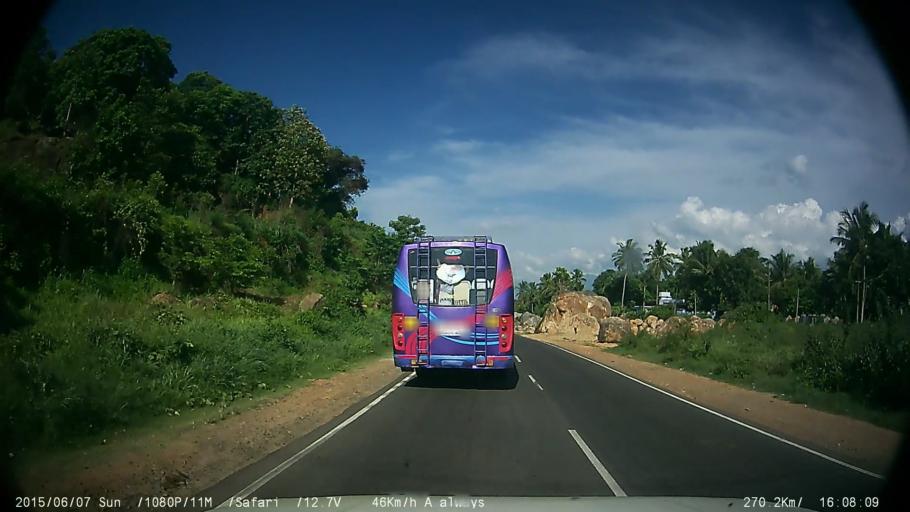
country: IN
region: Kerala
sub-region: Thrissur District
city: Chelakara
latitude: 10.5921
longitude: 76.4628
